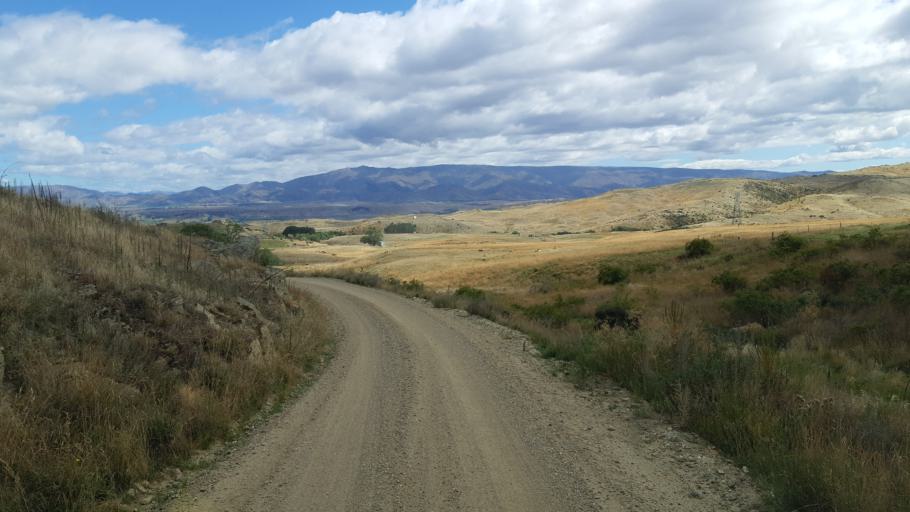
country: NZ
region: Otago
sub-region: Queenstown-Lakes District
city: Wanaka
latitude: -45.2173
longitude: 169.5639
